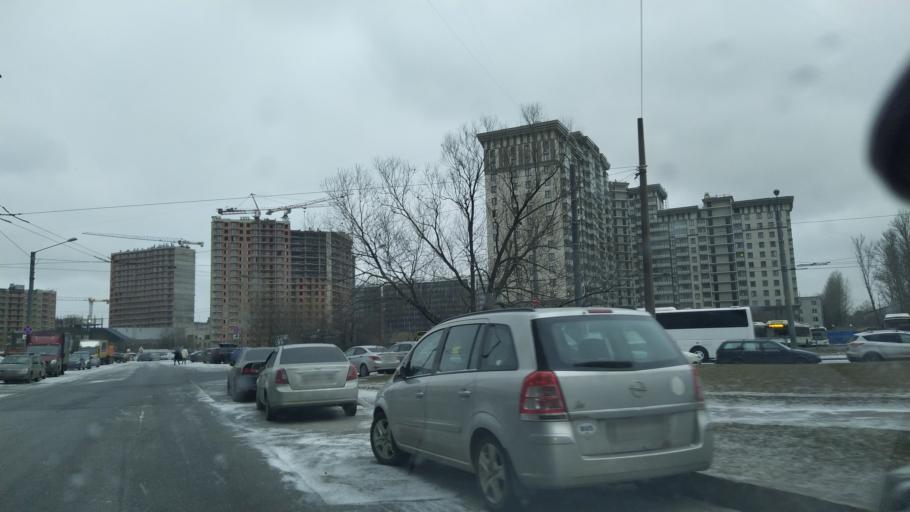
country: RU
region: St.-Petersburg
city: Kupchino
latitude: 59.8414
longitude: 30.3095
